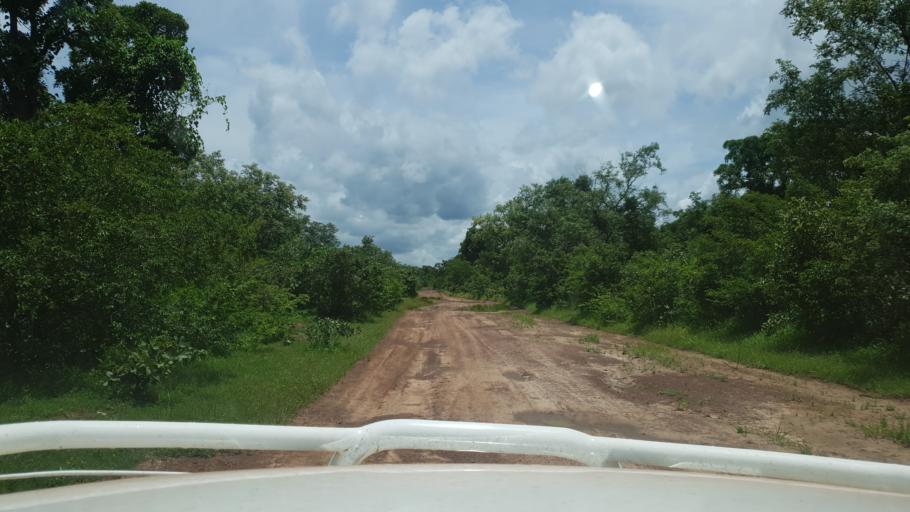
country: ML
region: Koulikoro
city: Banamba
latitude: 13.2009
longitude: -7.3368
